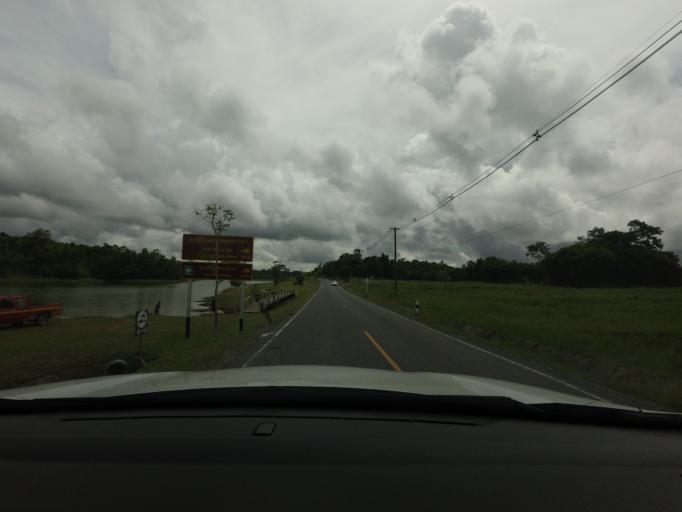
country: TH
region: Nakhon Nayok
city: Nakhon Nayok
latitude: 14.4296
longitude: 101.3694
